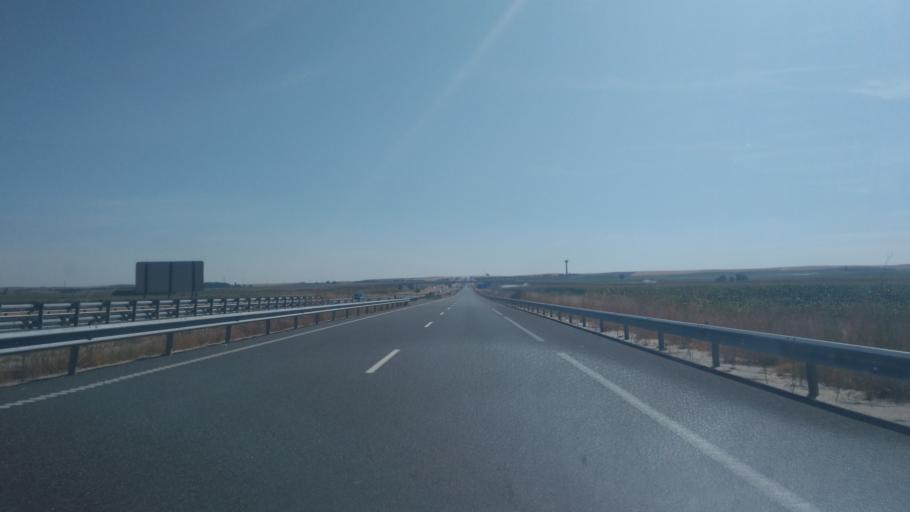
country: ES
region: Castille and Leon
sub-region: Provincia de Salamanca
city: Encinas de Abajo
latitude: 40.9307
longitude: -5.4441
